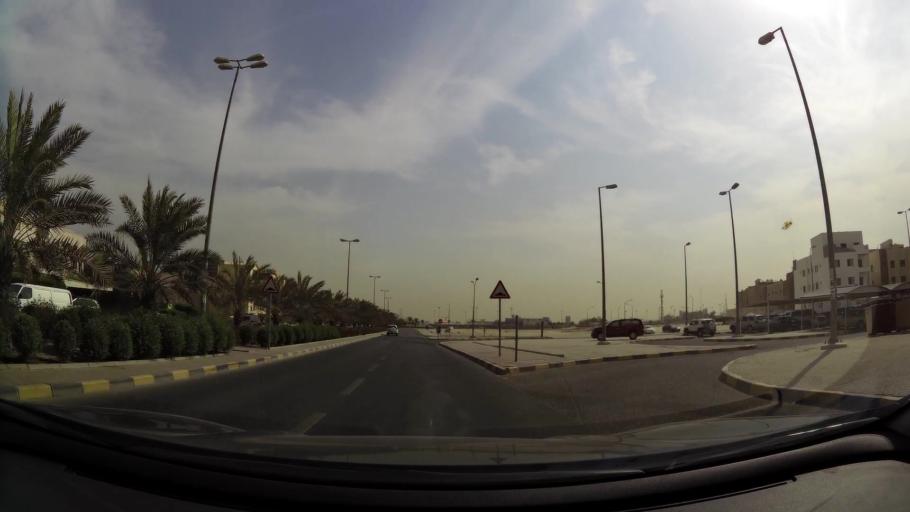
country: KW
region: Al Farwaniyah
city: Janub as Surrah
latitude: 29.2717
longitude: 47.9992
